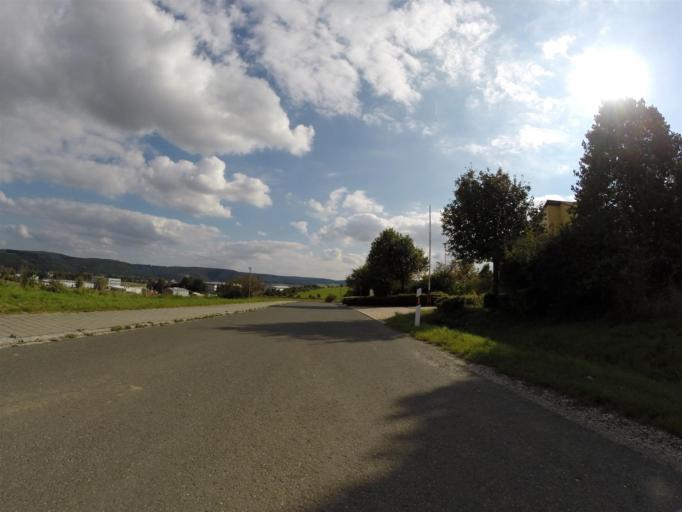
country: DE
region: Thuringia
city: Rothenstein
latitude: 50.8645
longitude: 11.5895
